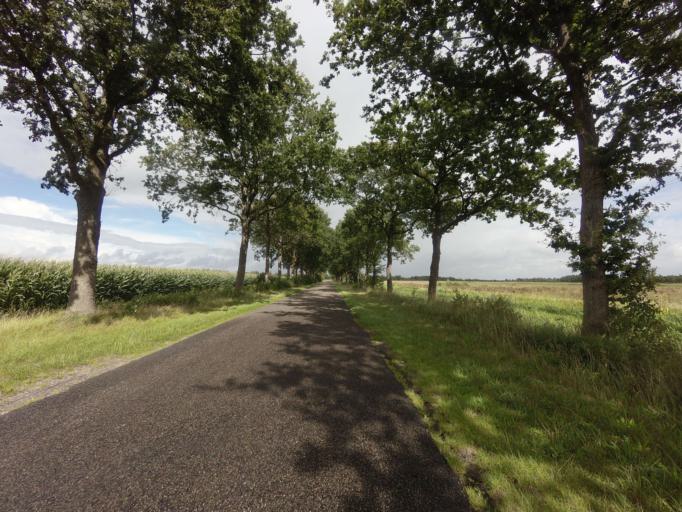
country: NL
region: Drenthe
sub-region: Gemeente Westerveld
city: Dwingeloo
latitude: 52.9840
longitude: 6.3703
